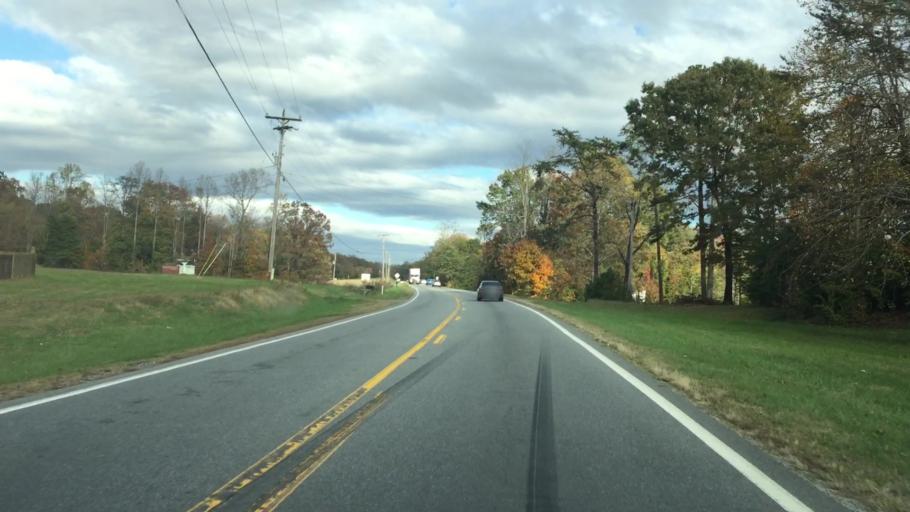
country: US
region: North Carolina
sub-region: Guilford County
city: Stokesdale
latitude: 36.2378
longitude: -80.0056
